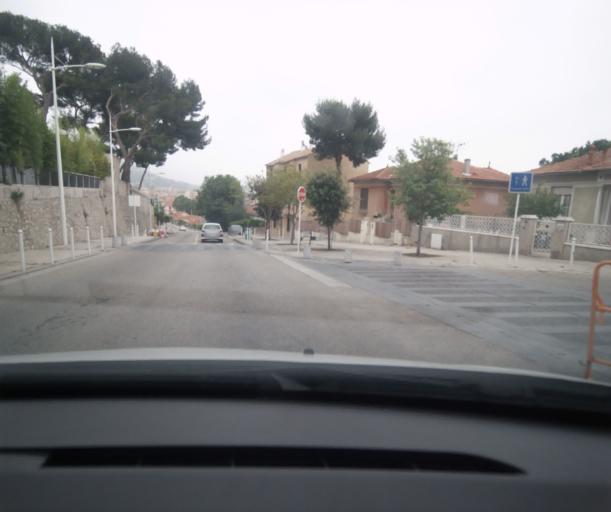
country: FR
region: Provence-Alpes-Cote d'Azur
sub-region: Departement du Var
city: La Valette-du-Var
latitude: 43.1338
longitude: 5.9750
